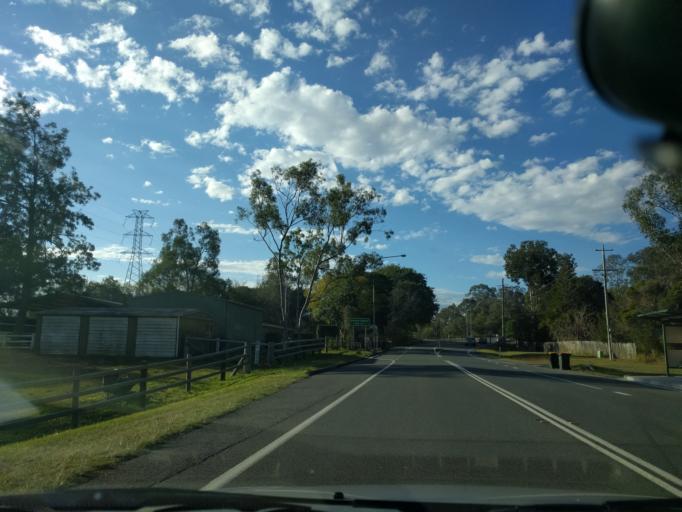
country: AU
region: Queensland
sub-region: Brisbane
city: Pullenvale
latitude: -27.5442
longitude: 152.8897
